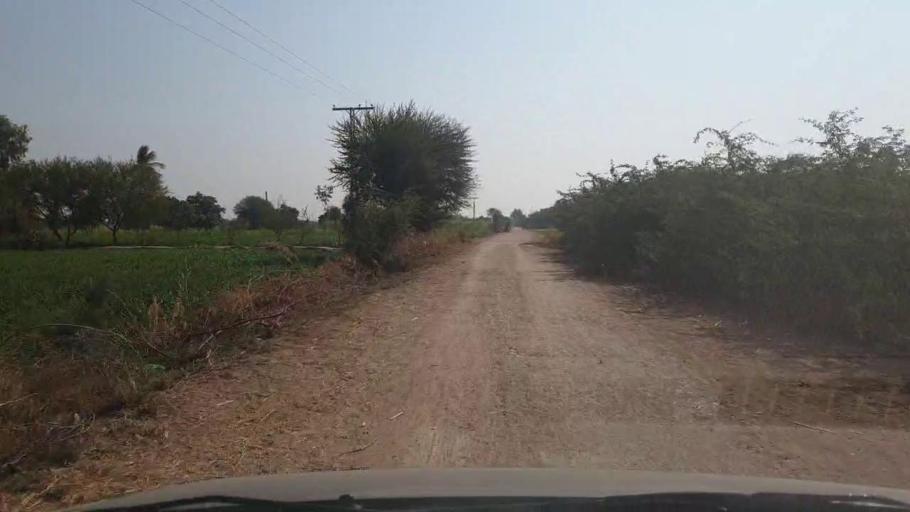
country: PK
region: Sindh
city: Mirwah Gorchani
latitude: 25.2544
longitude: 69.1148
